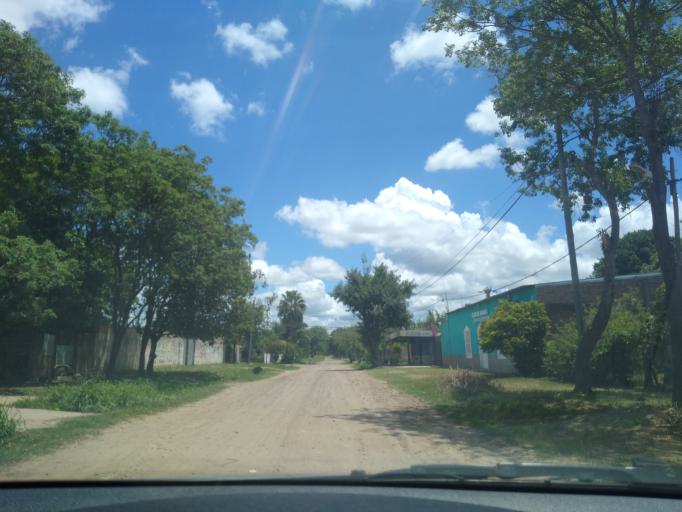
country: AR
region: Chaco
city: Barranqueras
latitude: -27.4730
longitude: -58.9321
